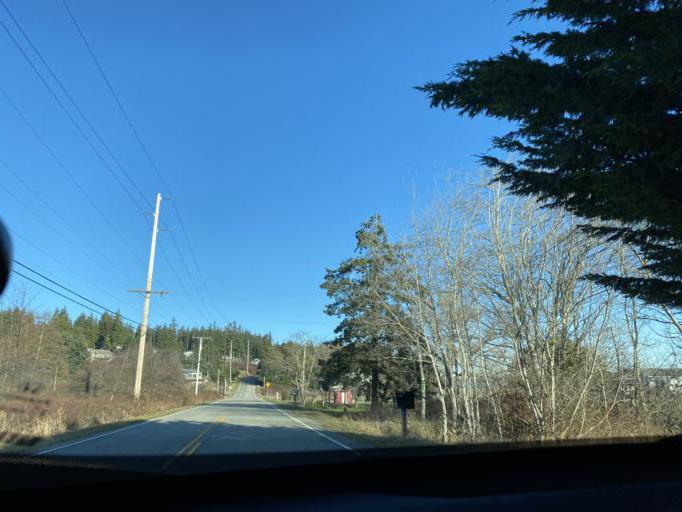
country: US
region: Washington
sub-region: Island County
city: Camano
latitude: 48.1085
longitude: -122.5695
